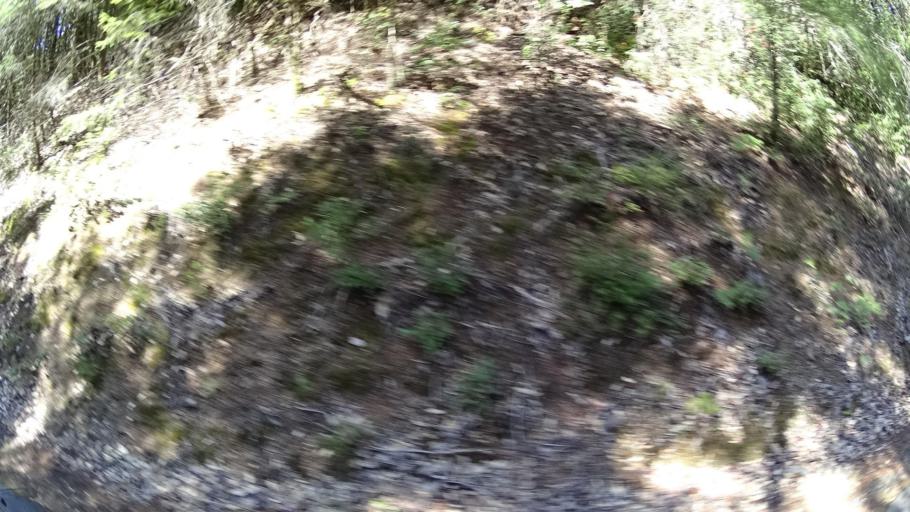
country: US
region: California
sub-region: Humboldt County
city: Redway
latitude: 40.2014
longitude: -124.1013
